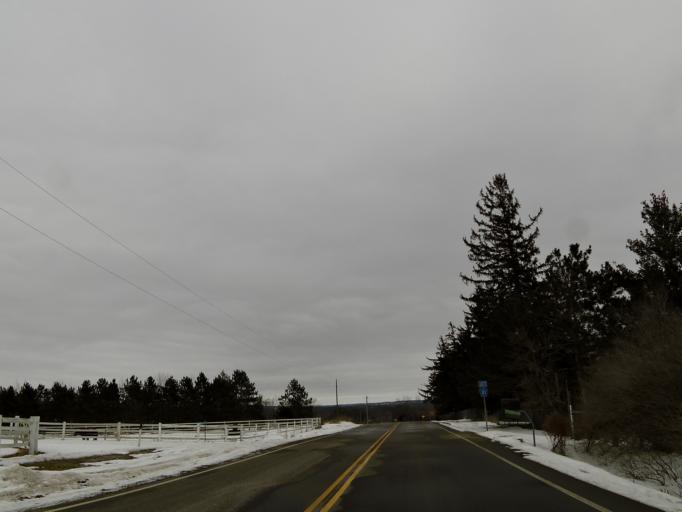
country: US
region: Wisconsin
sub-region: Pierce County
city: Prescott
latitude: 44.8191
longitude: -92.8064
